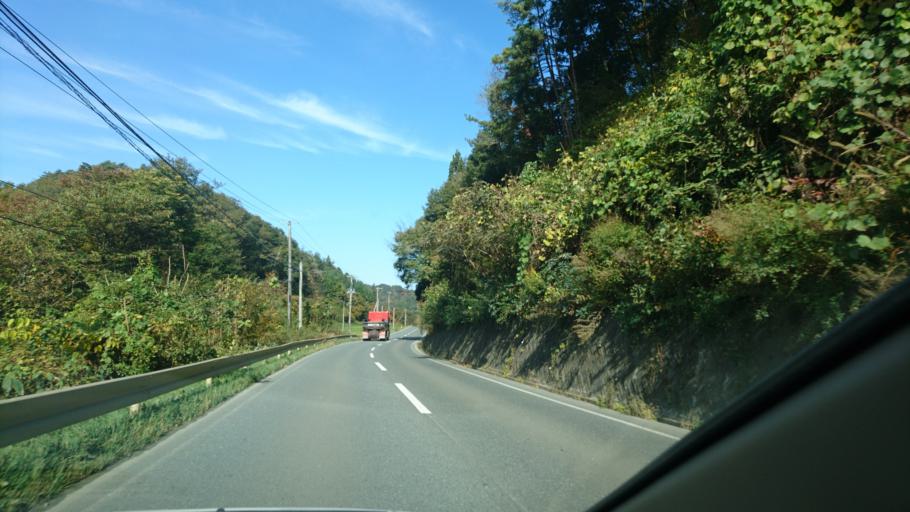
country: JP
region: Iwate
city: Mizusawa
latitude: 39.1437
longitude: 141.2453
